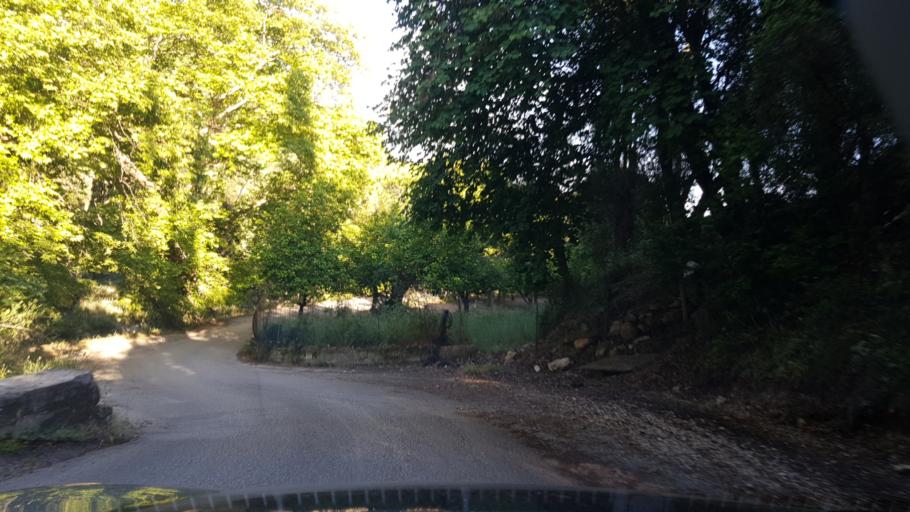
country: GR
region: Ionian Islands
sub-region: Lefkada
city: Nidri
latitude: 38.7223
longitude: 20.6930
